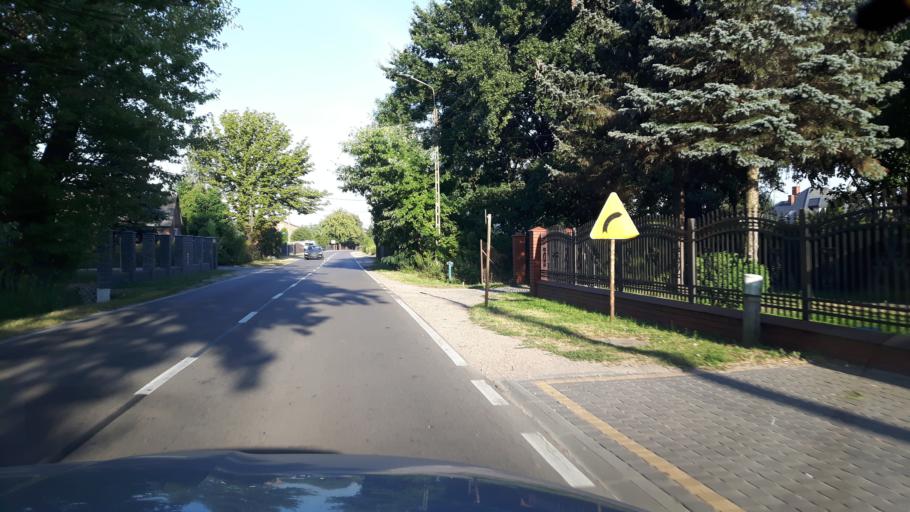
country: PL
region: Masovian Voivodeship
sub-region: Powiat wolominski
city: Slupno
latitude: 52.3647
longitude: 21.1517
